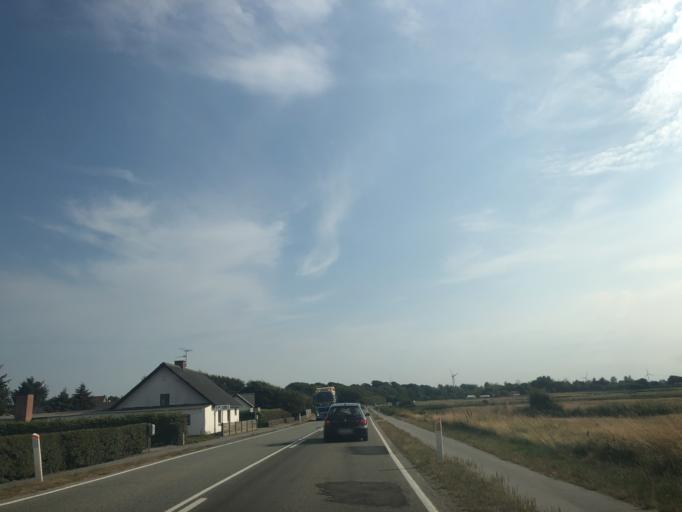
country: DK
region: North Denmark
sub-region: Morso Kommune
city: Nykobing Mors
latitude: 56.7883
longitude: 9.0438
